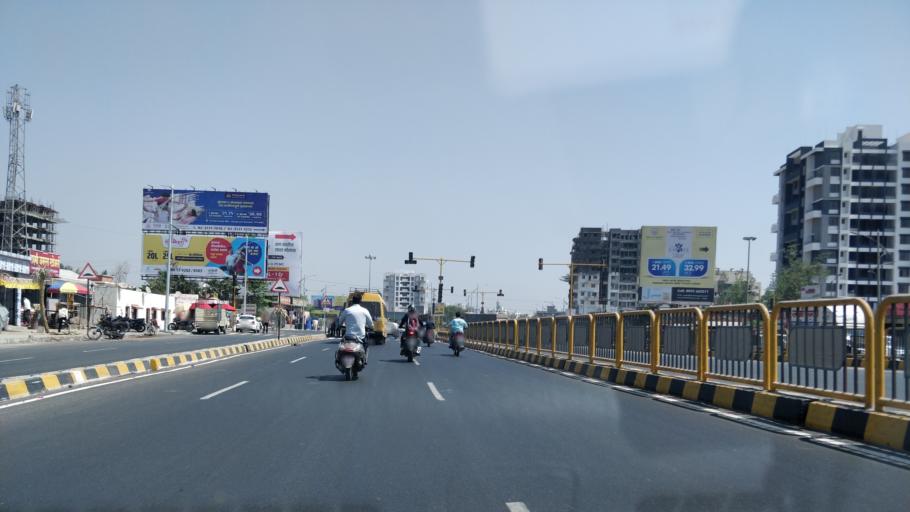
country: IN
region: Maharashtra
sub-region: Pune Division
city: Alandi
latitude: 18.6609
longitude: 73.8864
